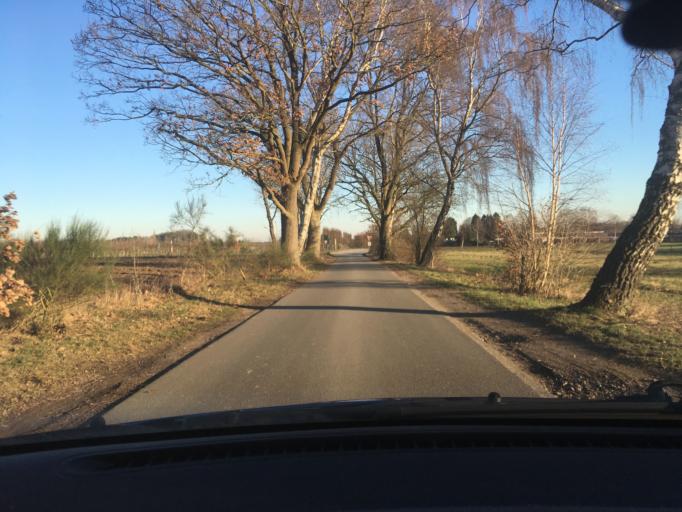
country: DE
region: Lower Saxony
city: Seevetal
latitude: 53.4019
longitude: 9.9622
